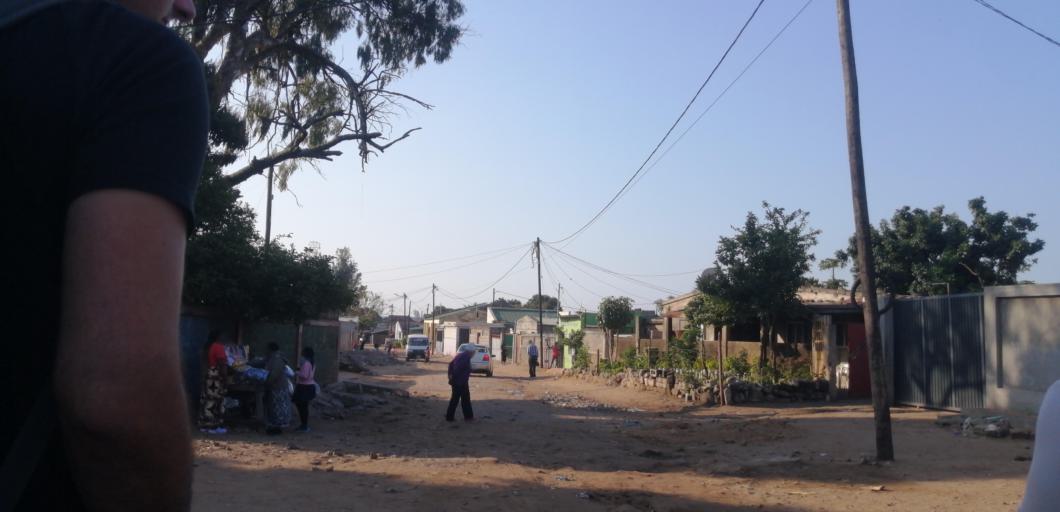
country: MZ
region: Maputo City
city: Maputo
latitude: -25.9538
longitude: 32.5691
